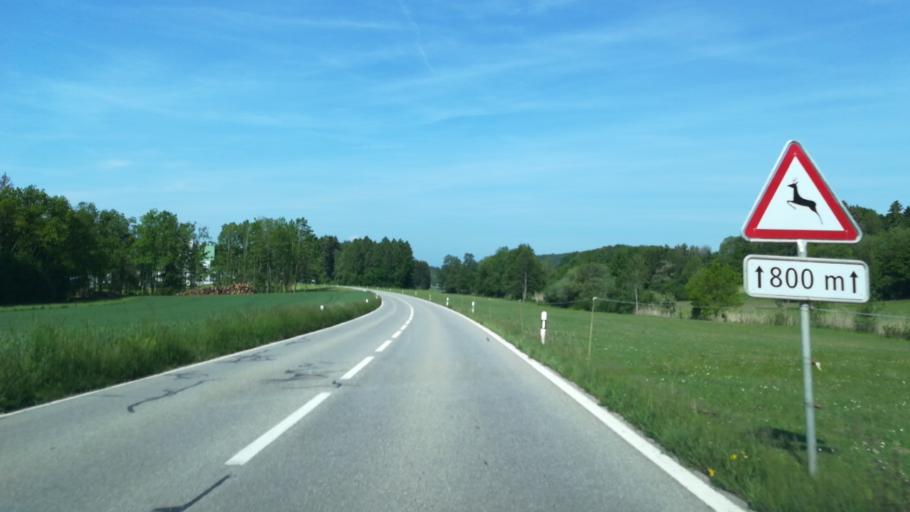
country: CH
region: Thurgau
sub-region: Weinfelden District
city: Wigoltingen
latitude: 47.6102
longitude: 9.0314
